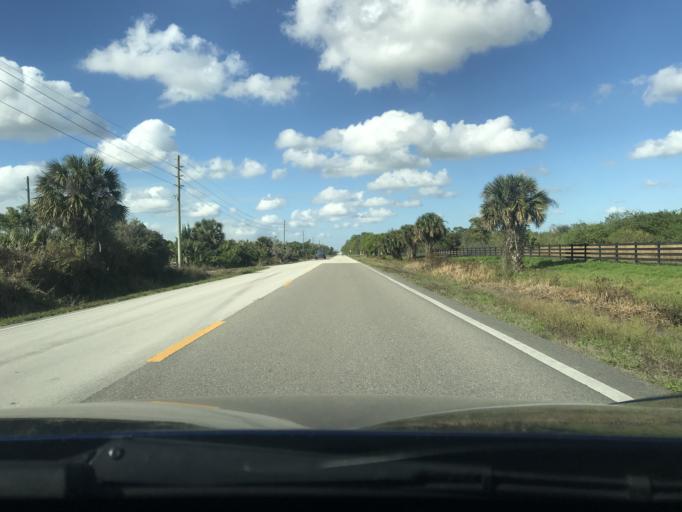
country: US
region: Florida
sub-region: Okeechobee County
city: Taylor Creek
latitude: 27.2188
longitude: -80.6942
